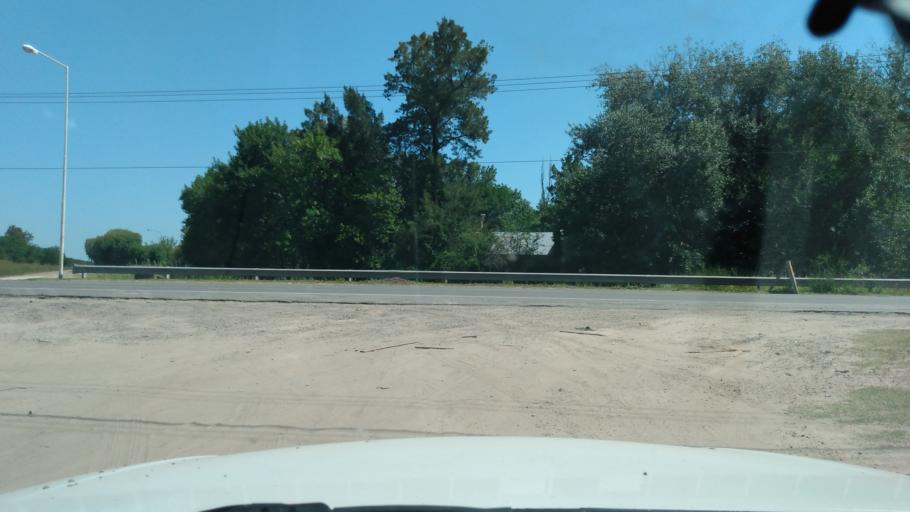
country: AR
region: Buenos Aires
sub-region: Partido de Lujan
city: Lujan
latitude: -34.5492
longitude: -59.1422
